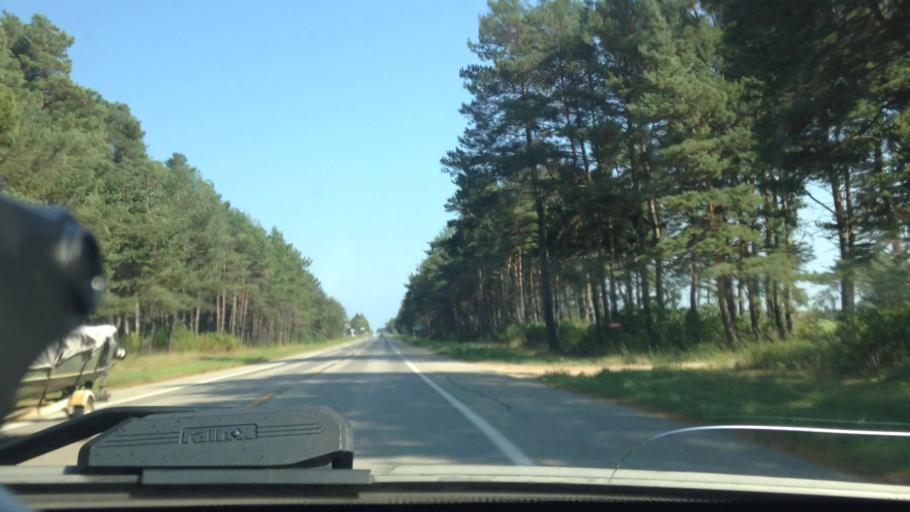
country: US
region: Michigan
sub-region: Luce County
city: Newberry
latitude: 46.3034
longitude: -85.4788
